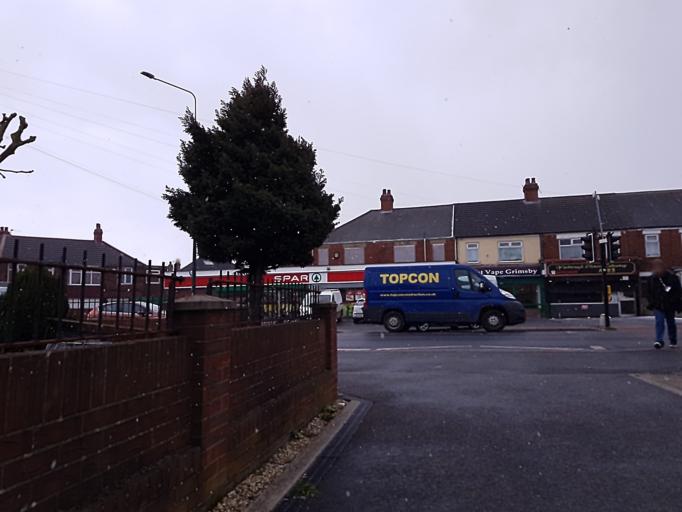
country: GB
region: England
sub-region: North East Lincolnshire
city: Grimbsy
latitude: 53.5628
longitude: -0.1113
